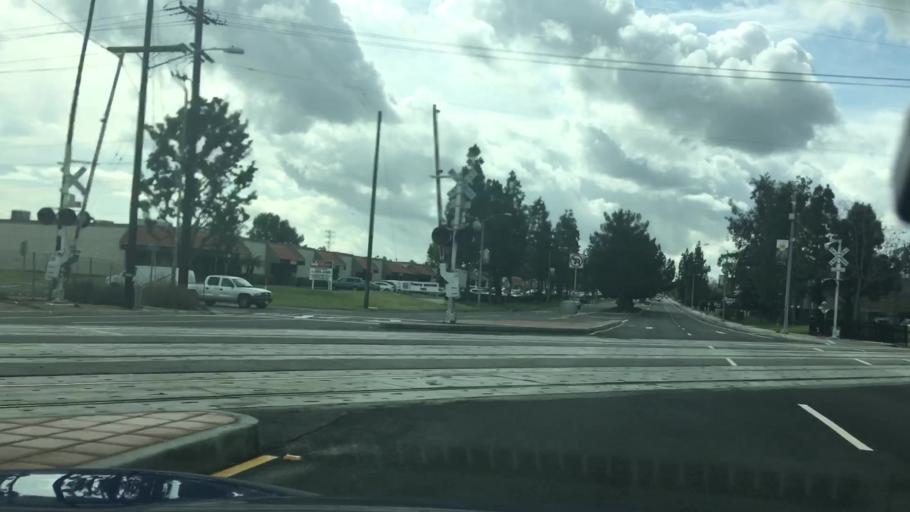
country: US
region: California
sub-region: Riverside County
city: Highgrove
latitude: 33.9979
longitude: -117.3485
